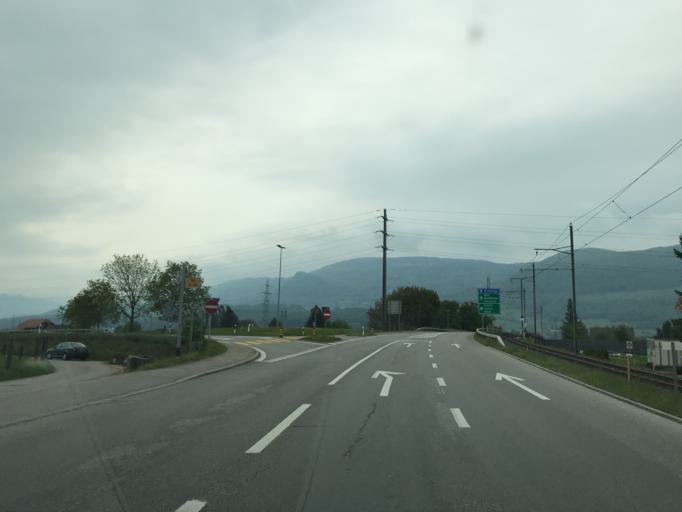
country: CH
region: Bern
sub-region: Oberaargau
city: Niederbipp
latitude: 47.2596
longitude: 7.7076
